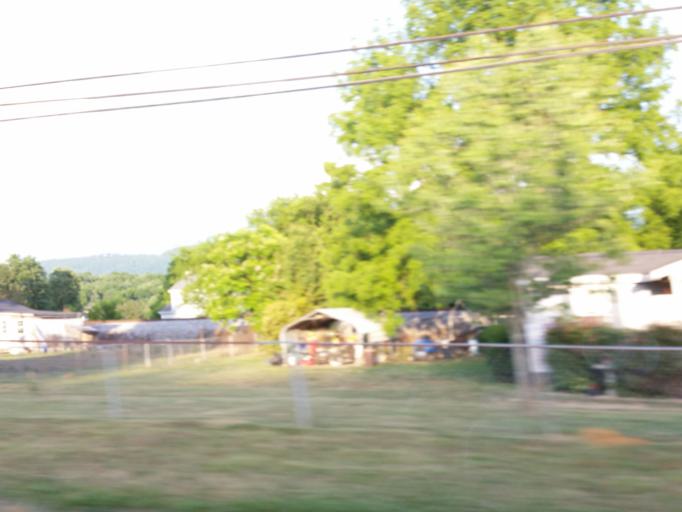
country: US
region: Georgia
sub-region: Dade County
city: Trenton
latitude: 34.9032
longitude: -85.4877
